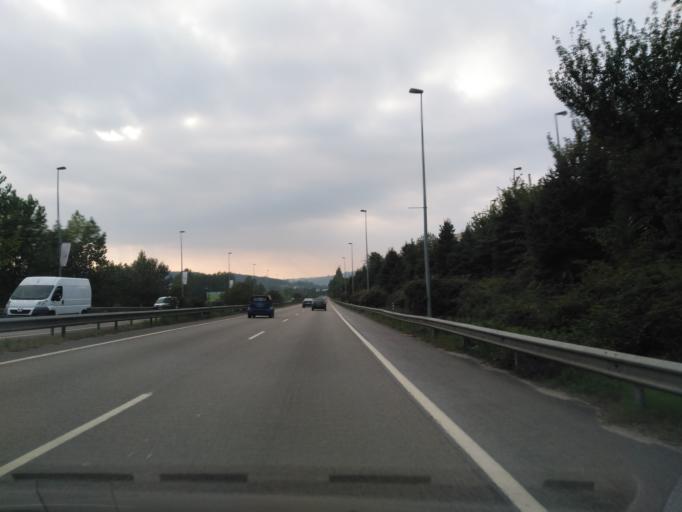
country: PT
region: Braga
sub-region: Guimaraes
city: Candoso
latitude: 41.4367
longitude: -8.3146
